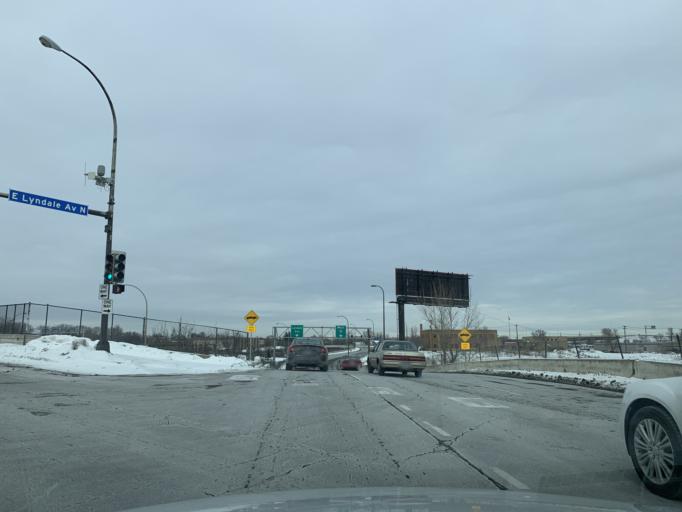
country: US
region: Minnesota
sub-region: Hennepin County
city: Minneapolis
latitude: 44.9872
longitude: -93.2881
